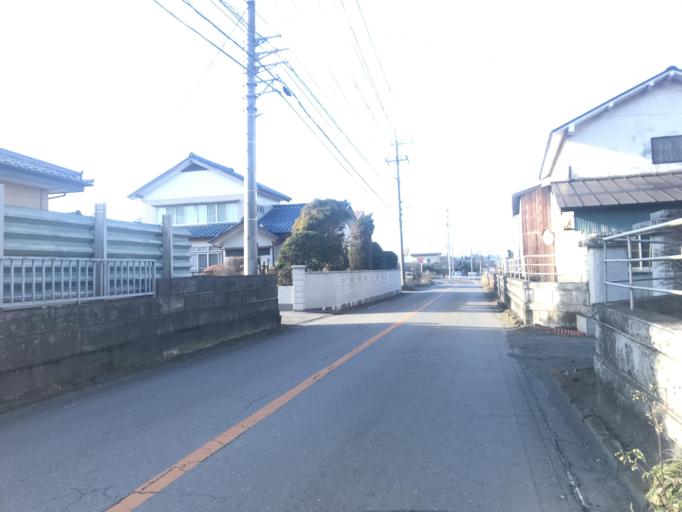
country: JP
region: Tochigi
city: Kaminokawa
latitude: 36.4260
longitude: 139.8724
